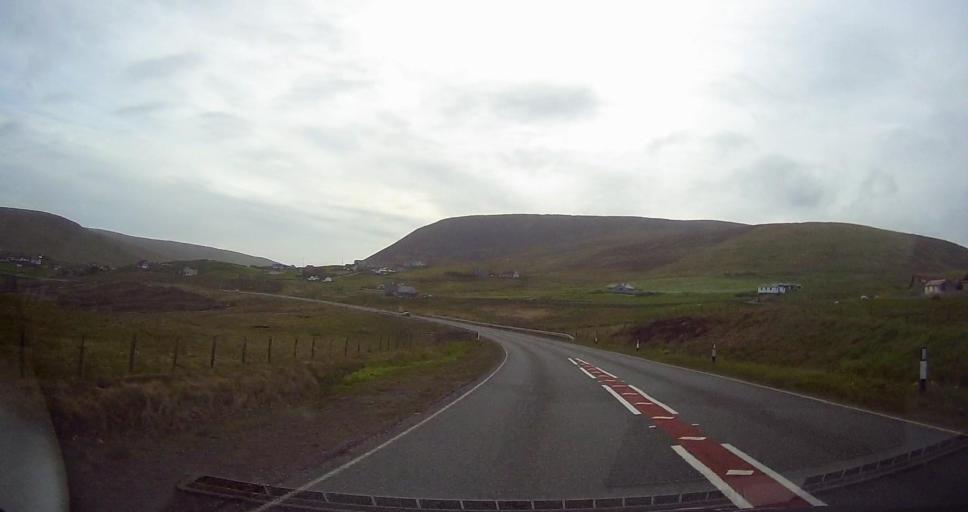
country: GB
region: Scotland
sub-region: Shetland Islands
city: Lerwick
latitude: 60.1043
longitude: -1.2255
